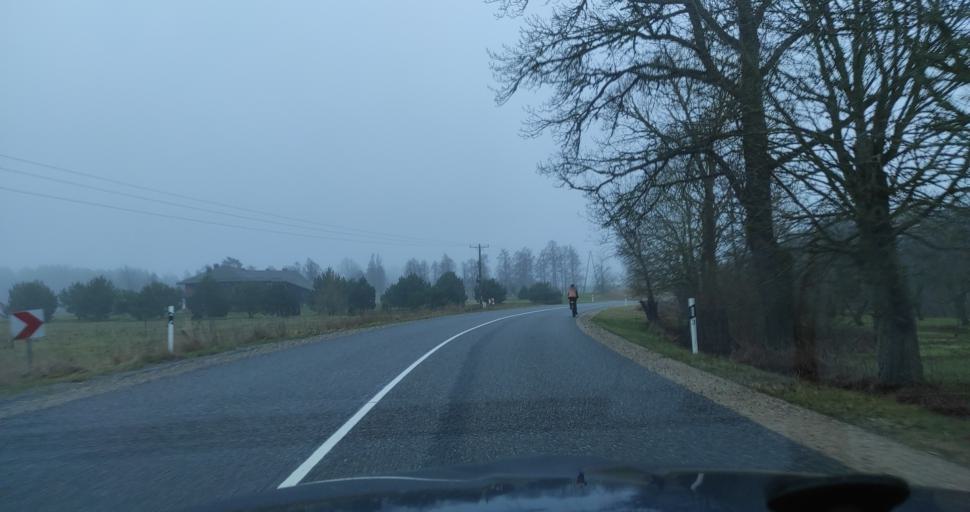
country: LV
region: Pavilostas
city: Pavilosta
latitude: 56.9791
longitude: 21.3612
